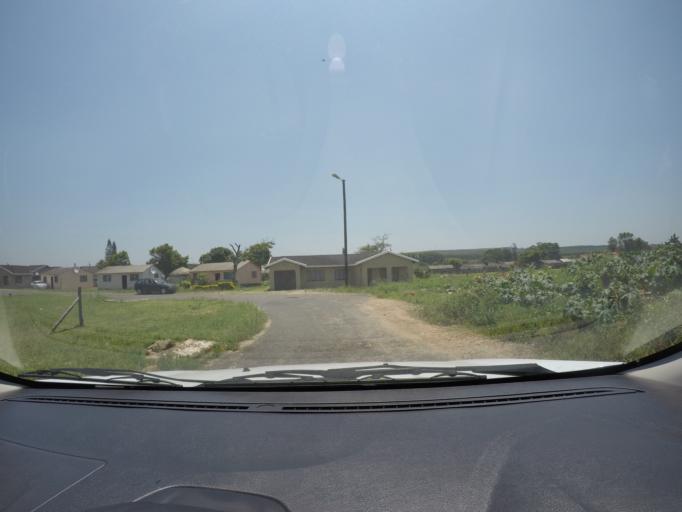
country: ZA
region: KwaZulu-Natal
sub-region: uThungulu District Municipality
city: eSikhawini
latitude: -28.8810
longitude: 31.8916
